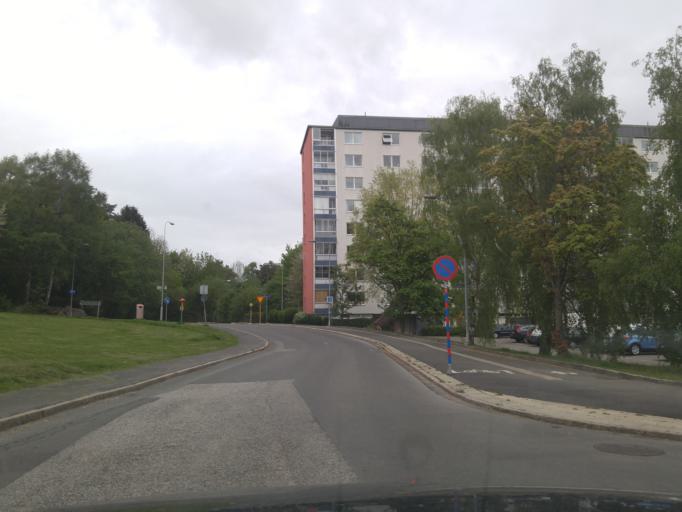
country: SE
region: Vaestra Goetaland
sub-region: Goteborg
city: Majorna
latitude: 57.6721
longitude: 11.9315
